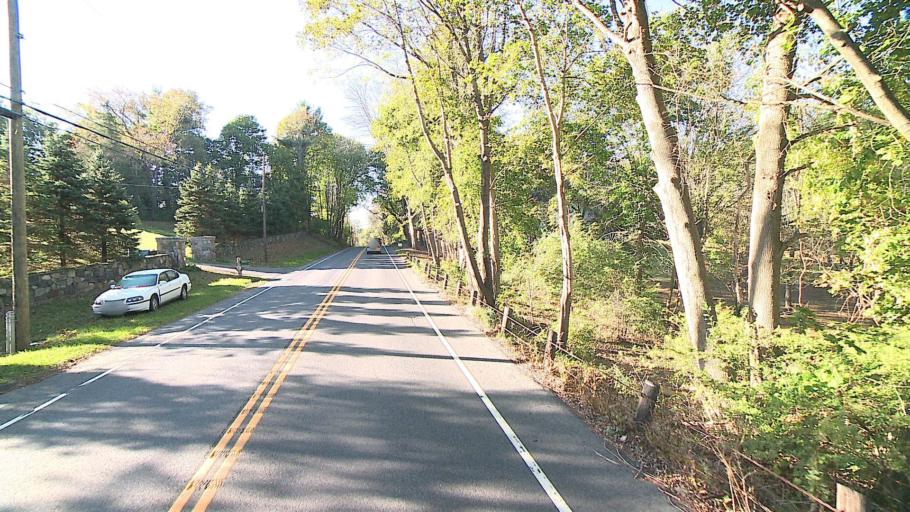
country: US
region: Connecticut
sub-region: Fairfield County
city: Bethel
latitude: 41.3391
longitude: -73.4161
